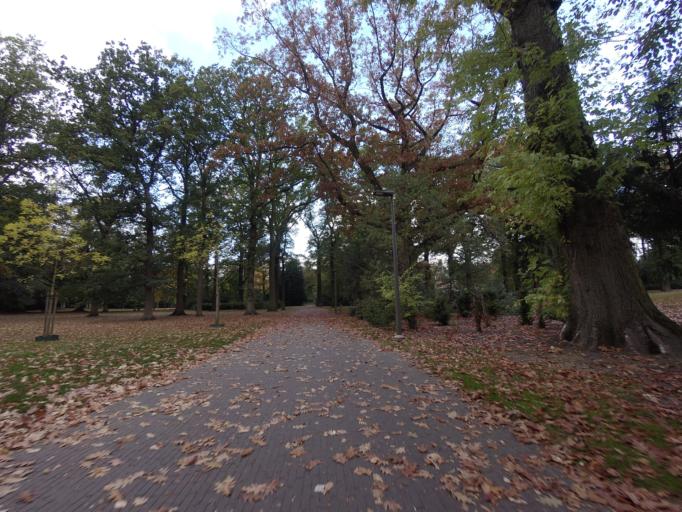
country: BE
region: Flanders
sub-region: Provincie Antwerpen
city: Antwerpen
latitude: 51.2476
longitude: 4.4477
